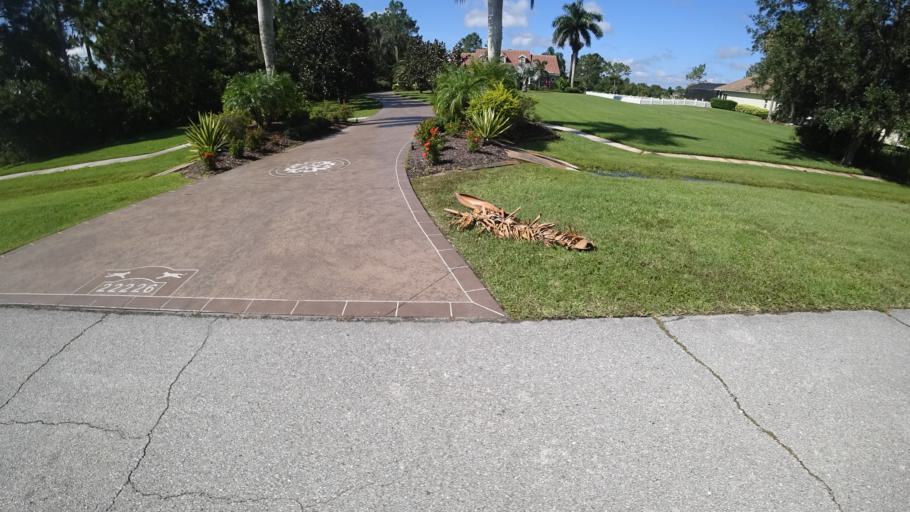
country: US
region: Florida
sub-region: Sarasota County
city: Fruitville
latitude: 27.3977
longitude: -82.3136
